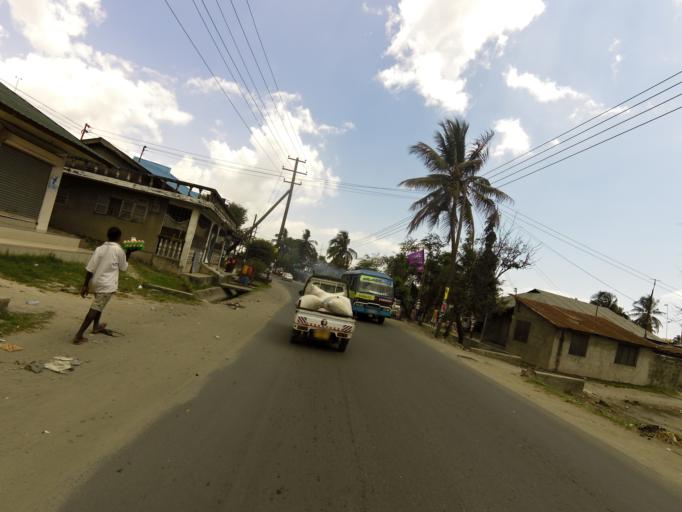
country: TZ
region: Dar es Salaam
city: Magomeni
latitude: -6.7964
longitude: 39.2480
